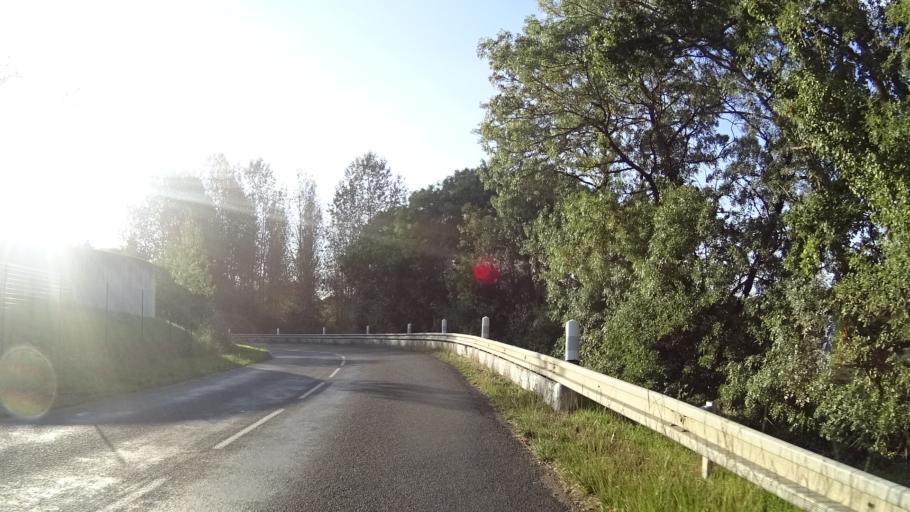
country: FR
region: Pays de la Loire
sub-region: Departement de Maine-et-Loire
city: Champtoceaux
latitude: 47.3385
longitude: -1.2474
